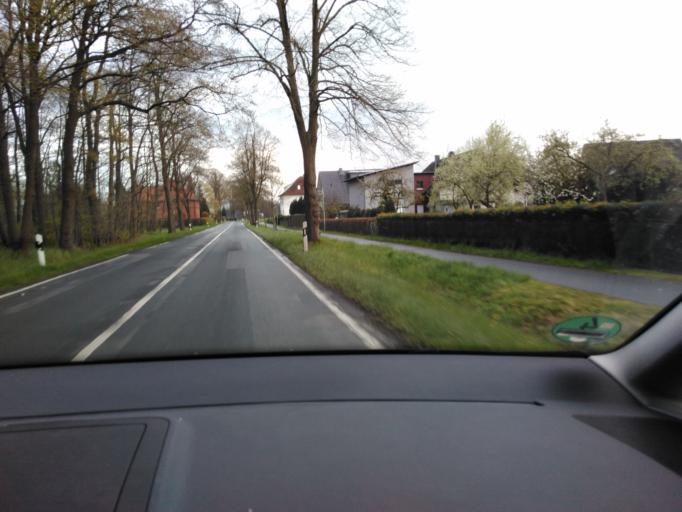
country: DE
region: North Rhine-Westphalia
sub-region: Regierungsbezirk Detmold
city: Verl
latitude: 51.9023
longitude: 8.4989
